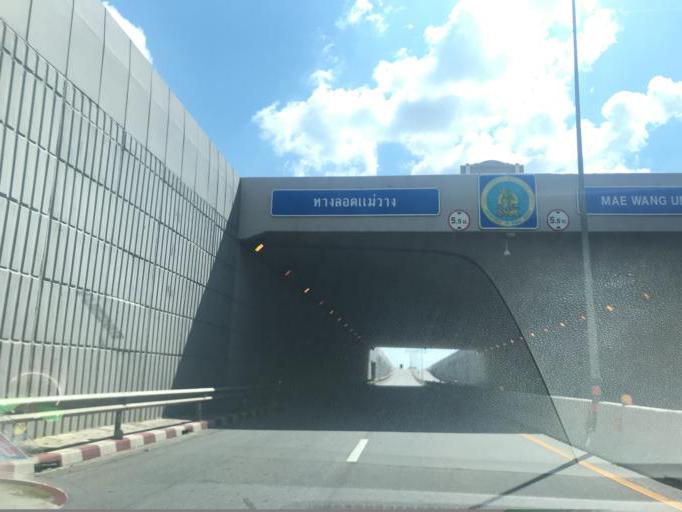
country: TH
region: Chiang Mai
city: Mae Wang
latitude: 18.6066
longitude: 98.8350
